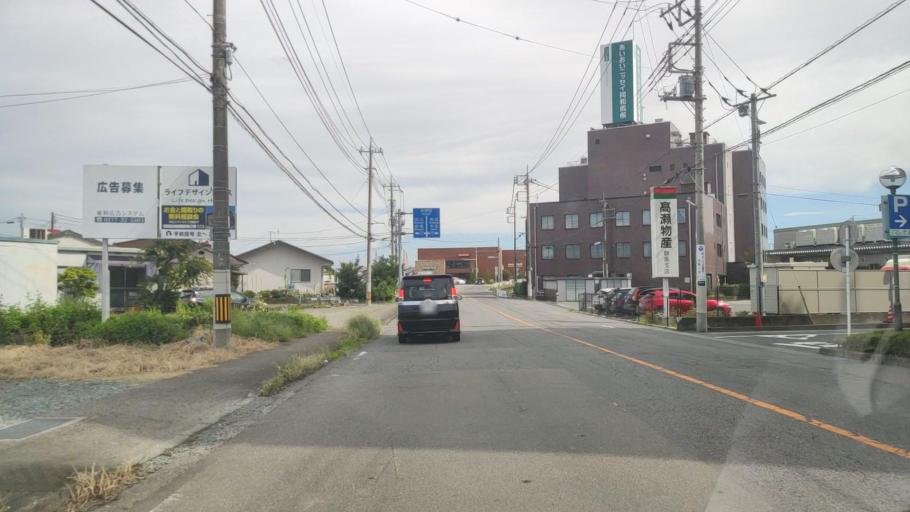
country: JP
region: Gunma
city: Takasaki
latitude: 36.3583
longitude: 139.0136
